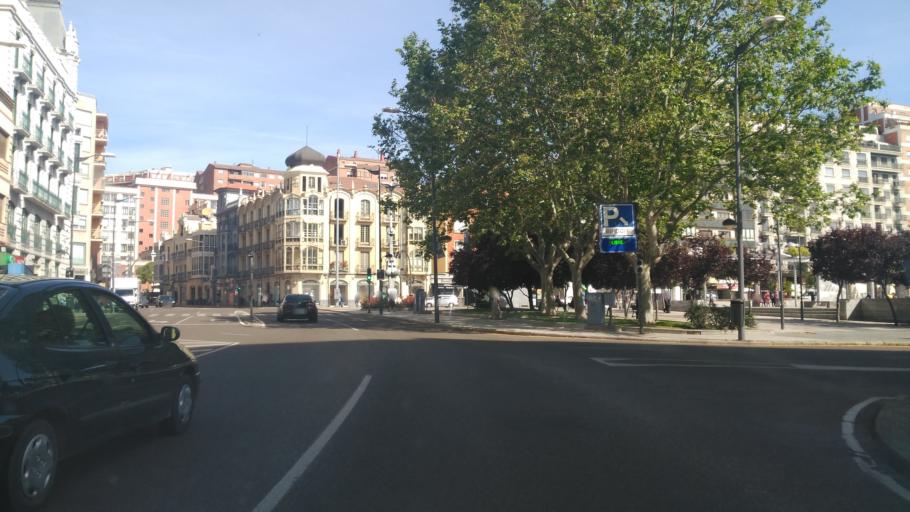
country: ES
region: Castille and Leon
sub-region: Provincia de Zamora
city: Zamora
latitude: 41.5067
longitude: -5.7405
